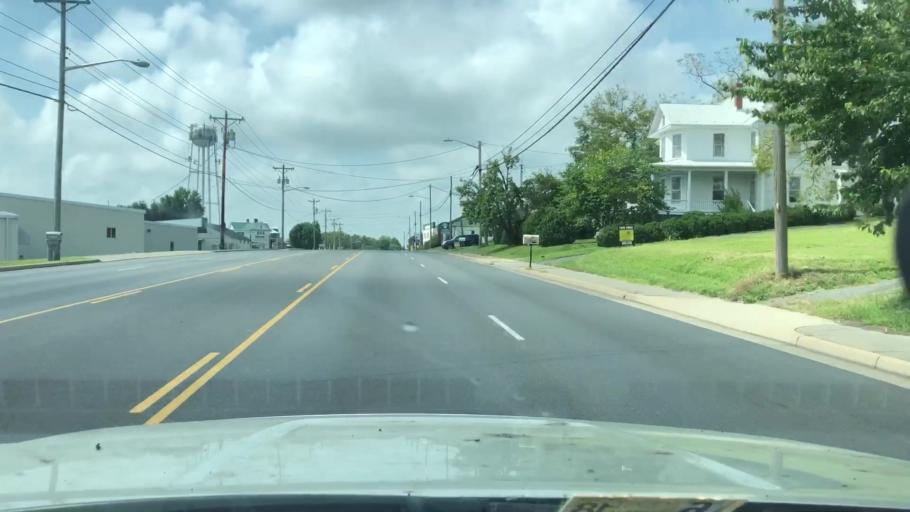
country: US
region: Virginia
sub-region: City of Harrisonburg
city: Harrisonburg
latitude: 38.4369
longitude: -78.8913
